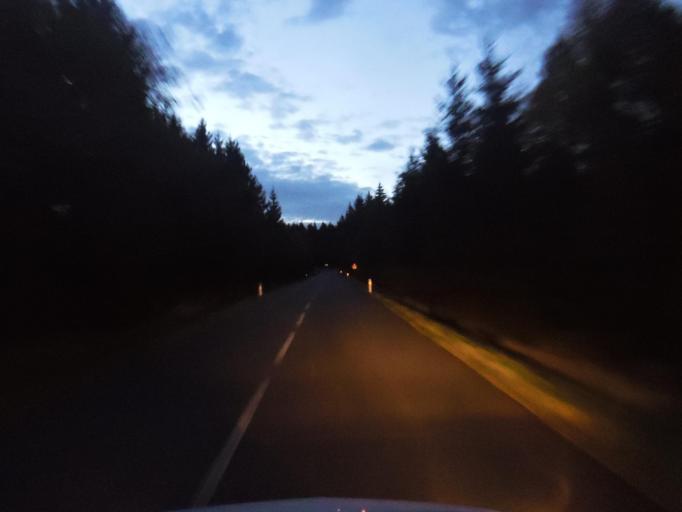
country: CZ
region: Ustecky
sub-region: Okres Chomutov
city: Kovarska
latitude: 50.4089
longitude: 13.0215
